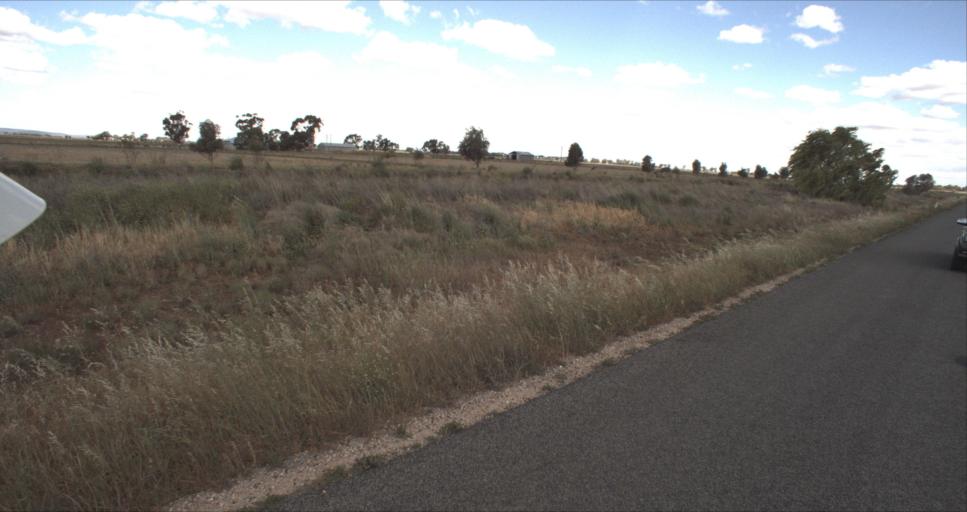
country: AU
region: New South Wales
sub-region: Leeton
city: Leeton
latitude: -34.4449
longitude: 146.2557
